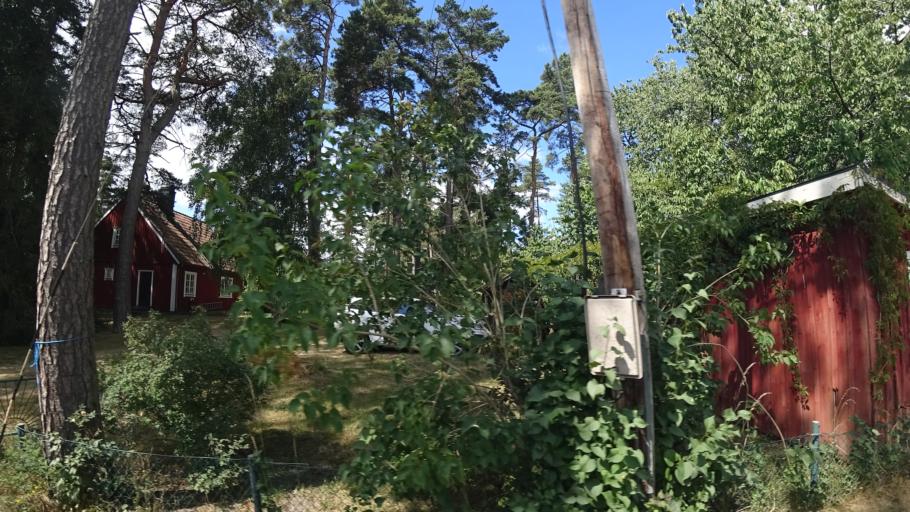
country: SE
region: Skane
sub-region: Kristianstads Kommun
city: Ahus
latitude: 55.9624
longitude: 14.2872
